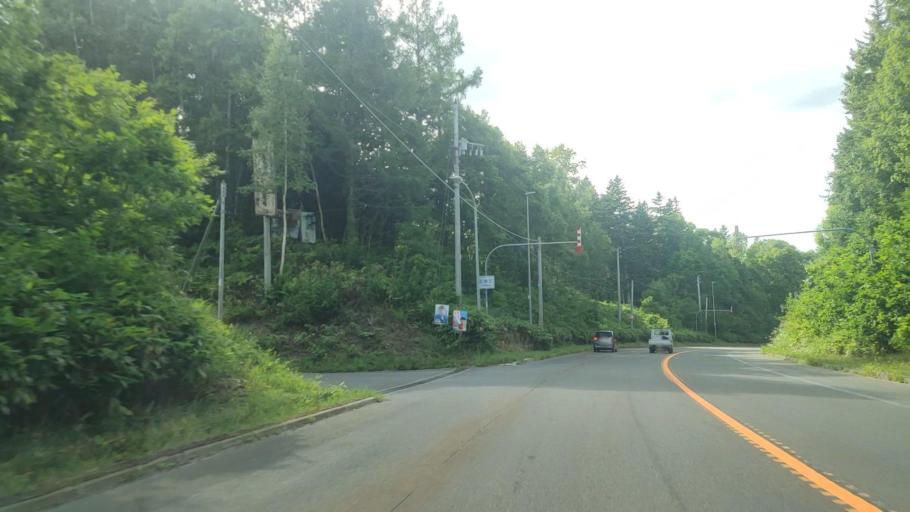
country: JP
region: Hokkaido
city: Nayoro
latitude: 44.3858
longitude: 142.3997
